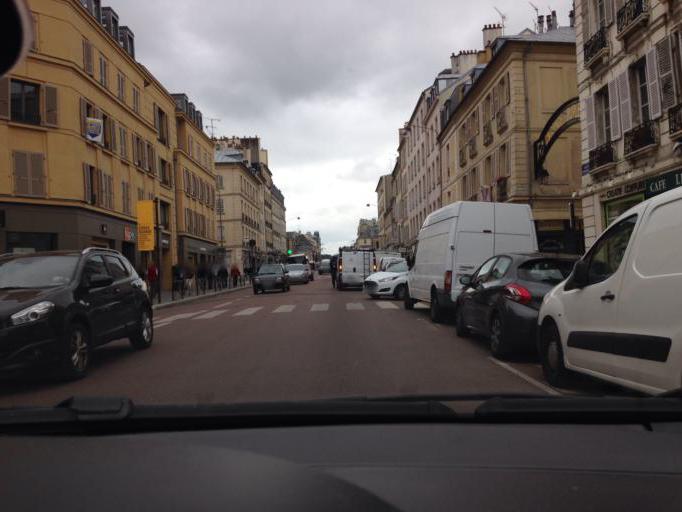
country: FR
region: Ile-de-France
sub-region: Departement des Yvelines
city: Versailles
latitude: 48.8083
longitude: 2.1330
